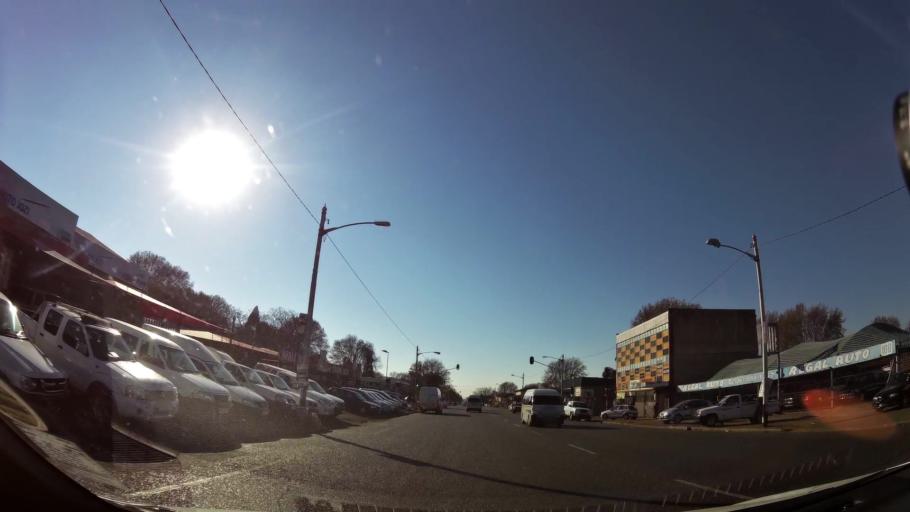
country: ZA
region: Gauteng
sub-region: City of Johannesburg Metropolitan Municipality
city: Johannesburg
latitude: -26.2056
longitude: 28.0782
